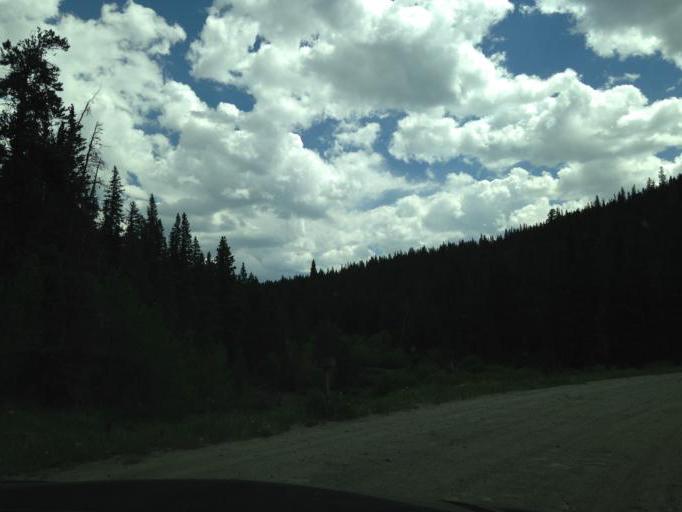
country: US
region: Colorado
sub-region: Park County
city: Fairplay
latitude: 39.3472
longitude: -105.9281
